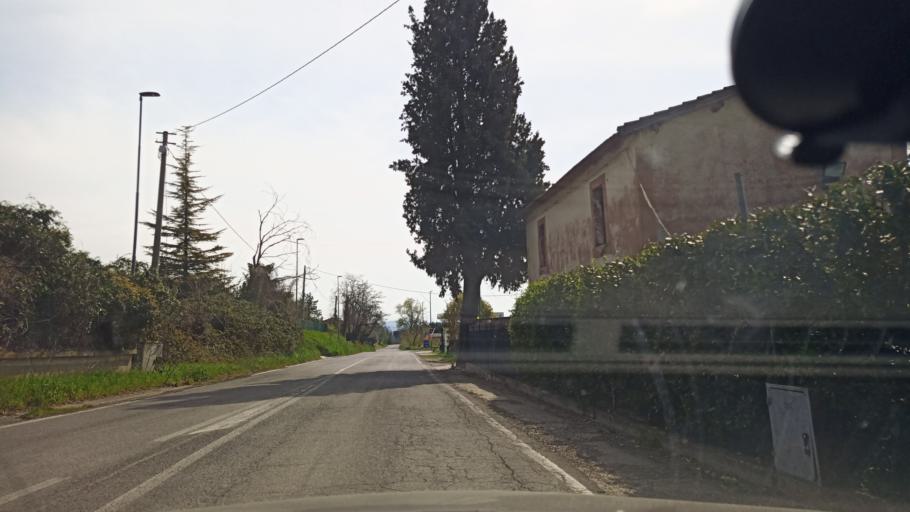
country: IT
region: Latium
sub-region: Provincia di Rieti
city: Cantalupo in Sabina
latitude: 42.3074
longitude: 12.6443
